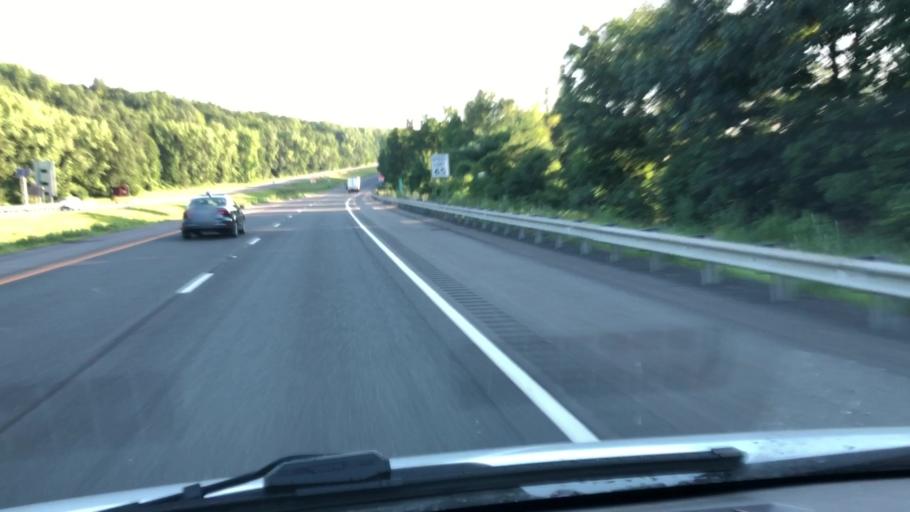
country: US
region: Massachusetts
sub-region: Franklin County
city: South Deerfield
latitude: 42.5305
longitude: -72.6277
